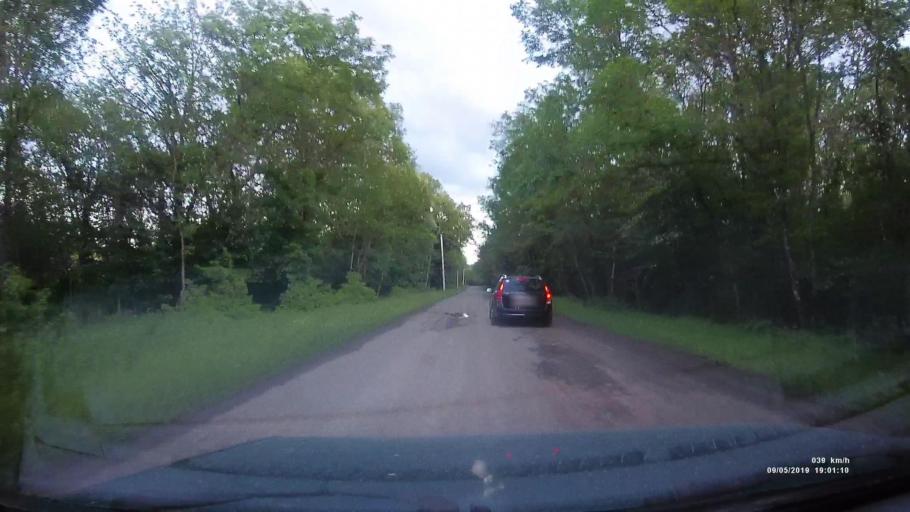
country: RU
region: Krasnodarskiy
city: Kanelovskaya
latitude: 46.7491
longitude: 39.1418
